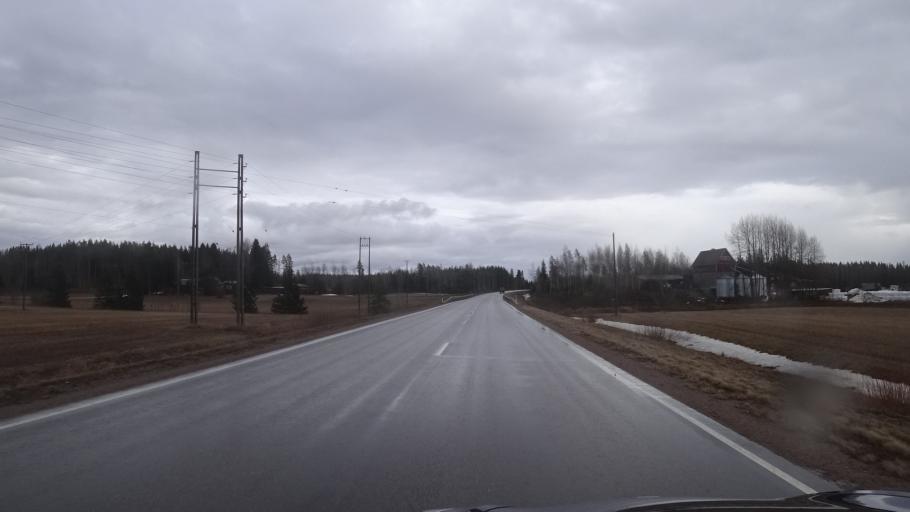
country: FI
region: Kymenlaakso
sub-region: Kouvola
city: Elimaeki
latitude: 60.7126
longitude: 26.4636
